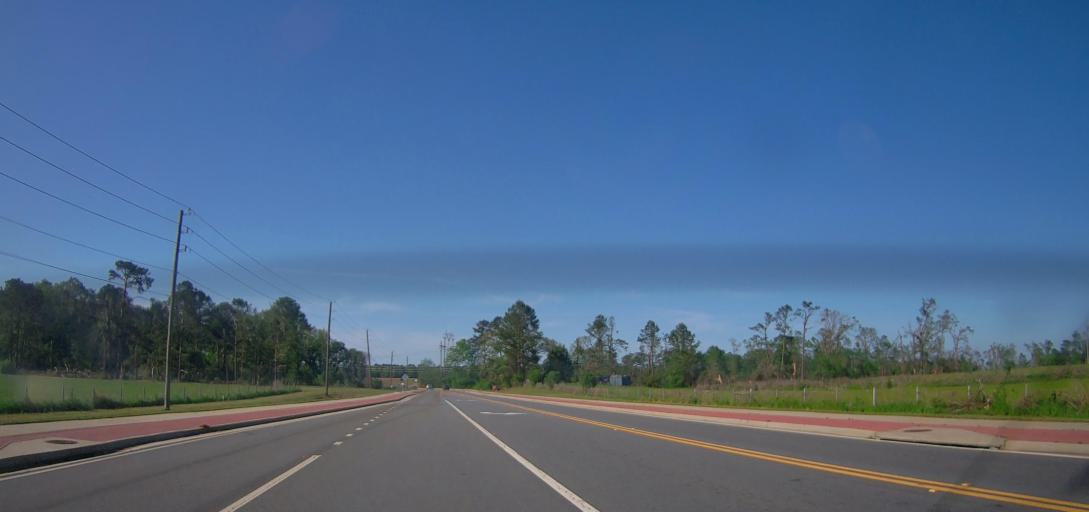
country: US
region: Georgia
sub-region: Houston County
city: Robins Air Force Base
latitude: 32.5528
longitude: -83.5856
